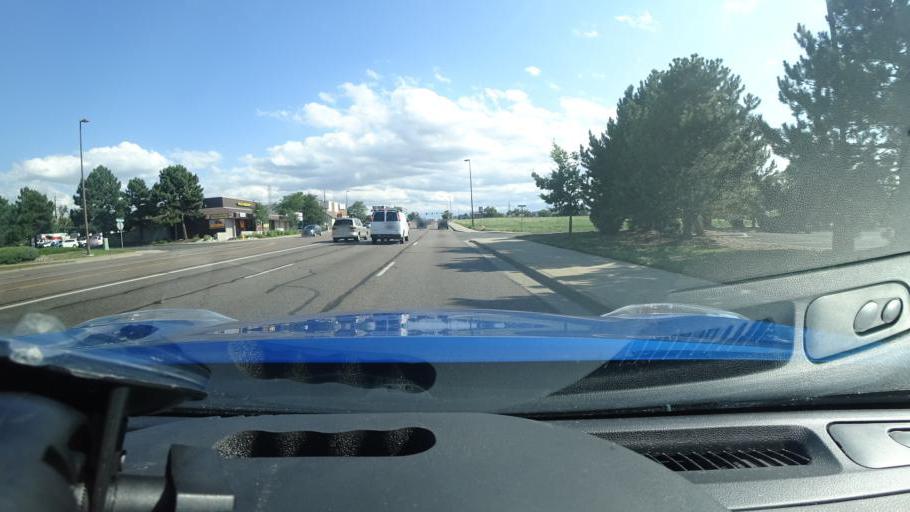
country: US
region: Colorado
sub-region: Adams County
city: Aurora
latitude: 39.6843
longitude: -104.8661
